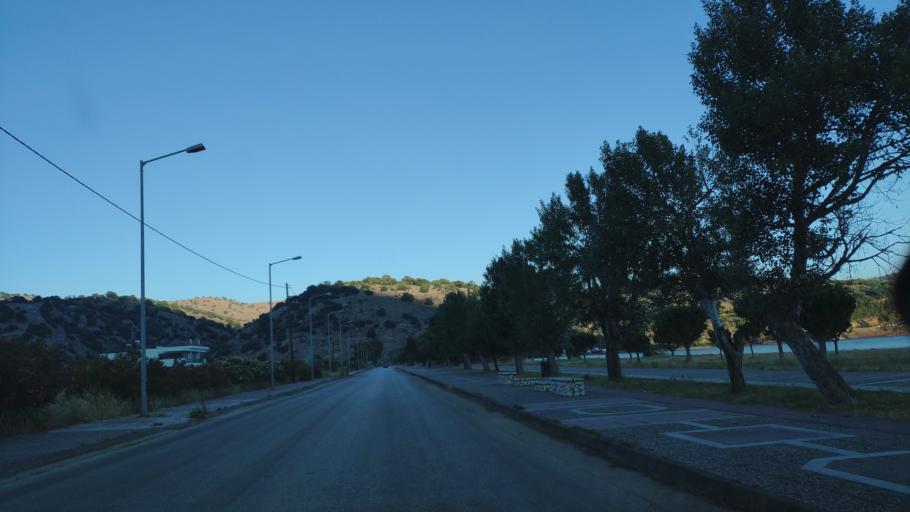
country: GR
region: West Greece
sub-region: Nomos Aitolias kai Akarnanias
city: Astakos
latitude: 38.5343
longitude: 21.0918
